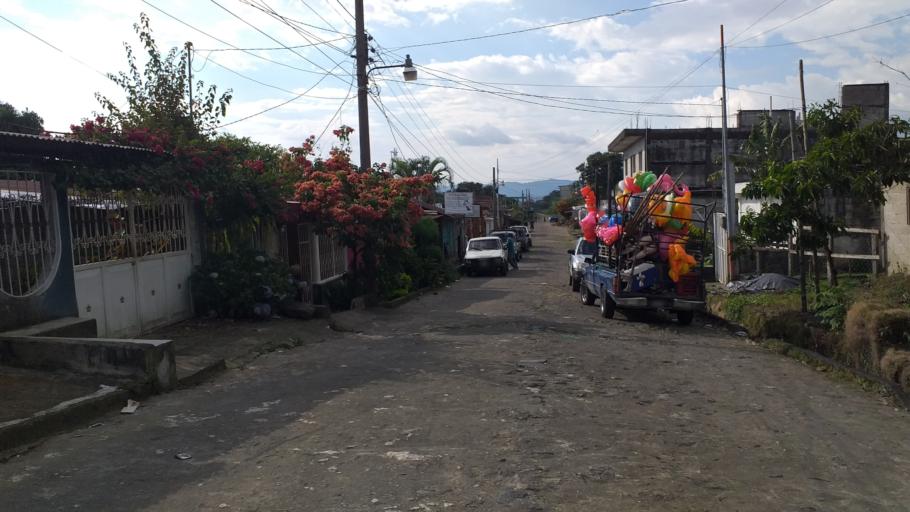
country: GT
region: Suchitepeque
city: Pueblo Nuevo
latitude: 14.6430
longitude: -91.5582
